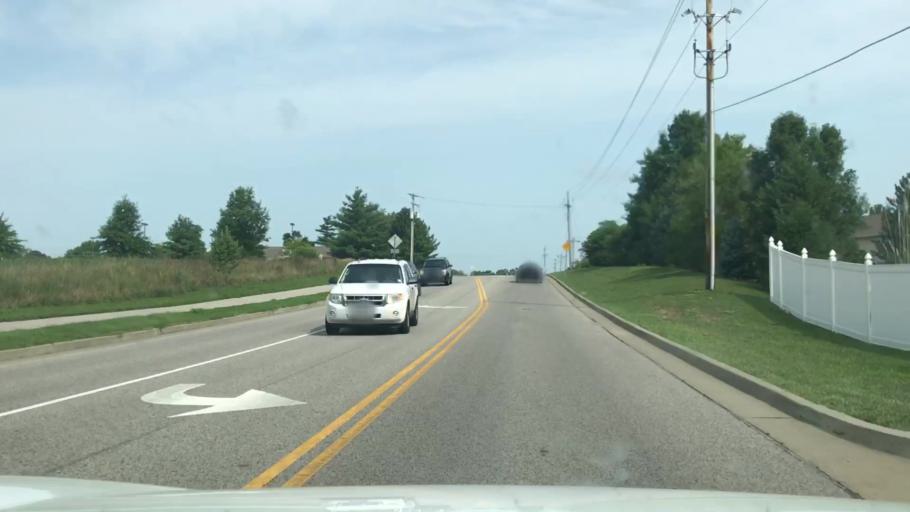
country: US
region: Missouri
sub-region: Saint Charles County
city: Cottleville
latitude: 38.7250
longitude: -90.6433
